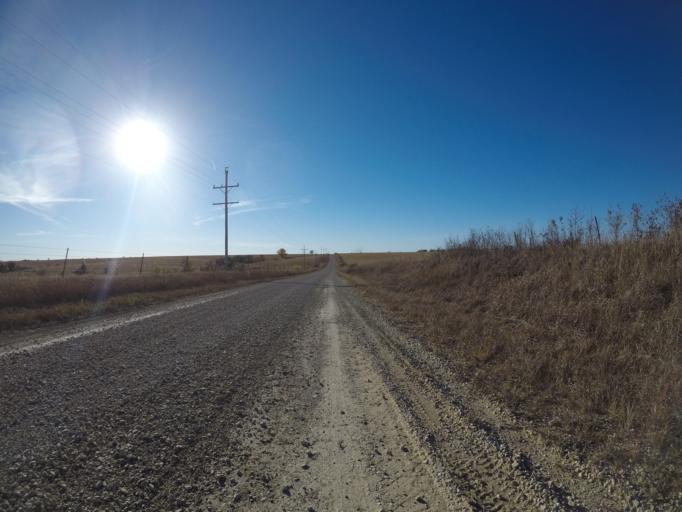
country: US
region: Kansas
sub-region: Riley County
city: Ogden
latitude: 39.2616
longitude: -96.7123
